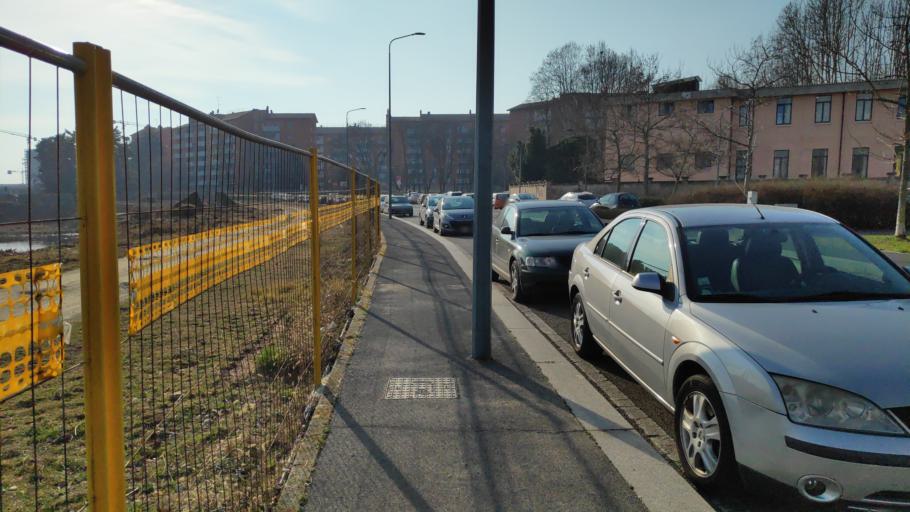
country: IT
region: Lombardy
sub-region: Citta metropolitana di Milano
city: Linate
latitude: 45.4437
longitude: 9.2472
